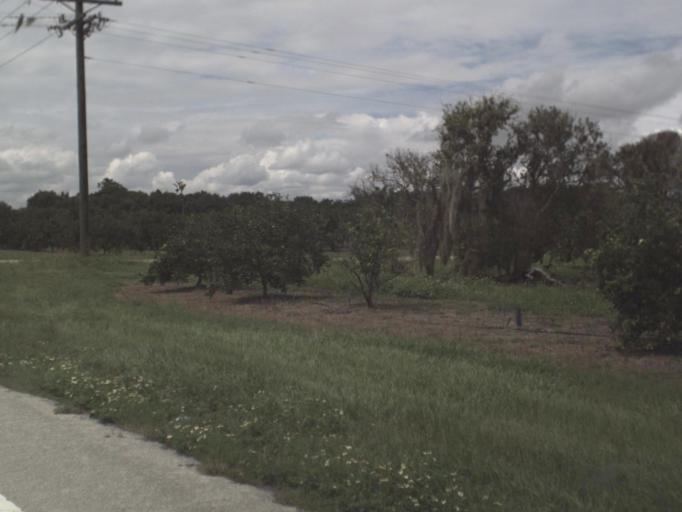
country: US
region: Florida
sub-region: Hardee County
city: Bowling Green
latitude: 27.5948
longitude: -81.8747
